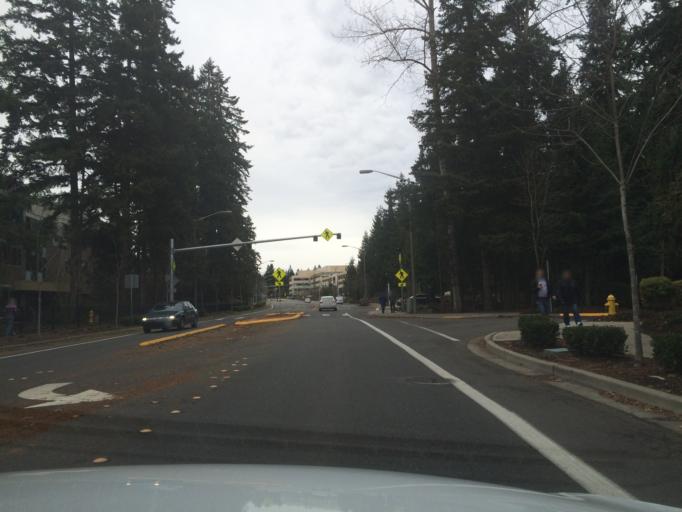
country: US
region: Washington
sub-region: King County
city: Redmond
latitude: 47.6404
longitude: -122.1366
